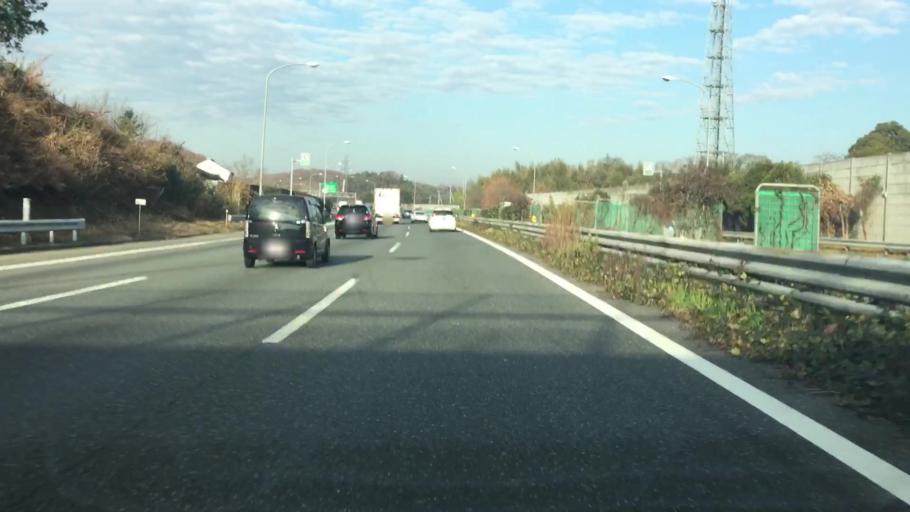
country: JP
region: Saitama
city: Ogawa
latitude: 36.0650
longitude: 139.3227
